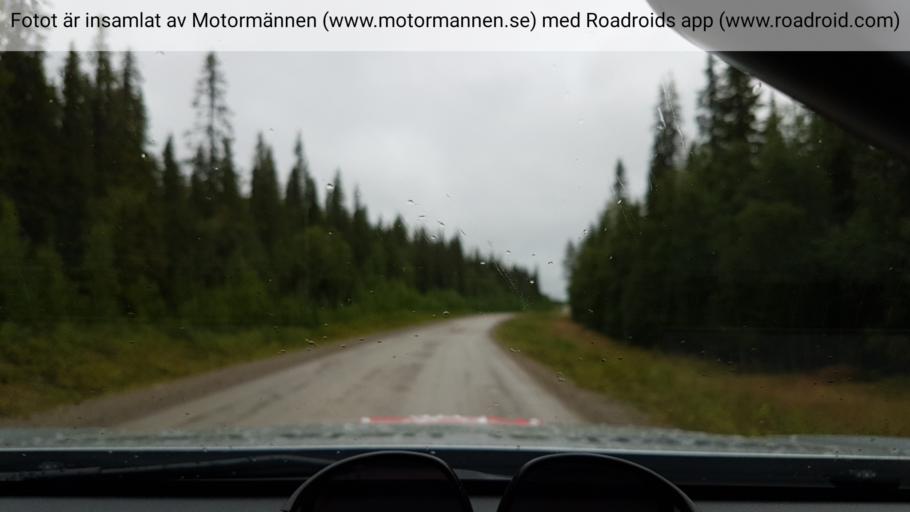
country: SE
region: Vaesterbotten
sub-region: Storumans Kommun
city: Storuman
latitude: 64.9194
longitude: 17.2623
